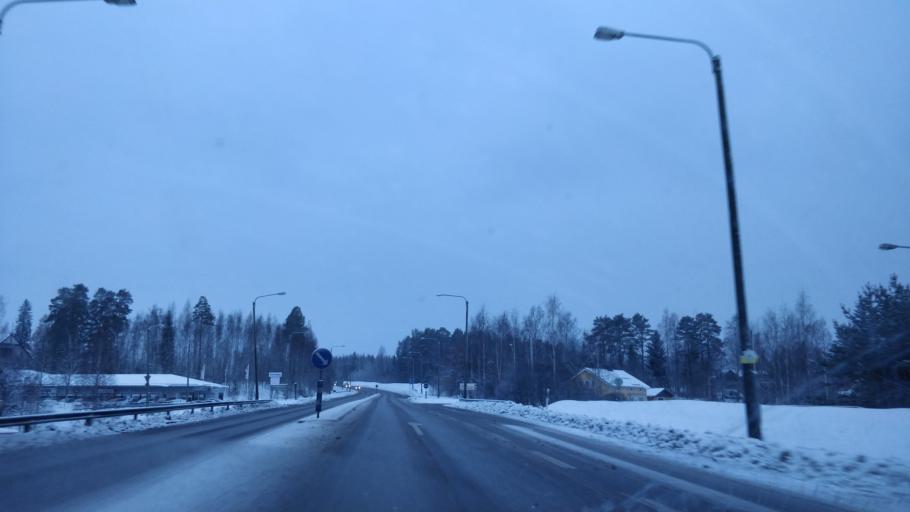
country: FI
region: Central Finland
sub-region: Saarijaervi-Viitasaari
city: Viitasaari
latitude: 63.0666
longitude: 25.8530
